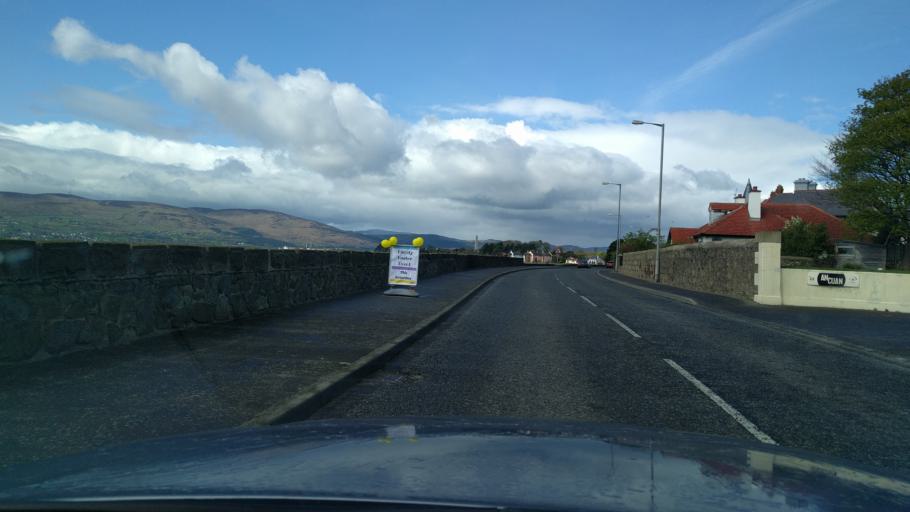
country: GB
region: Northern Ireland
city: Rostrevor
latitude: 54.0961
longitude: -6.1944
